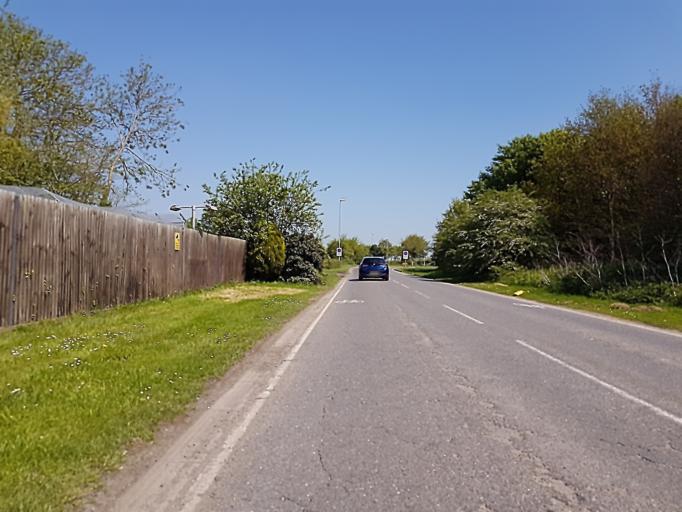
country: GB
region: England
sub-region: Cambridgeshire
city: Harston
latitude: 52.1206
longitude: 0.0560
